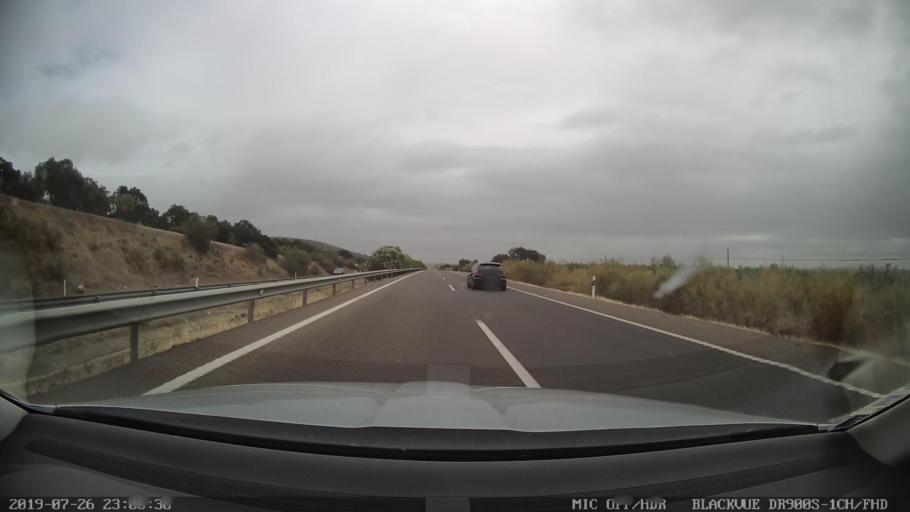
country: ES
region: Extremadura
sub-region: Provincia de Badajoz
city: San Pedro de Merida
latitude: 38.9602
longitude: -6.1583
